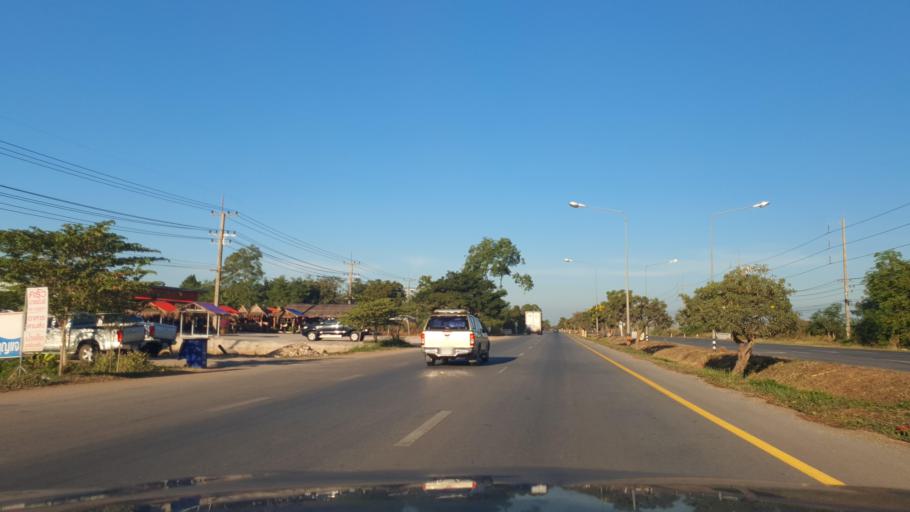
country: TH
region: Phitsanulok
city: Phitsanulok
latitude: 16.8593
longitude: 100.3080
